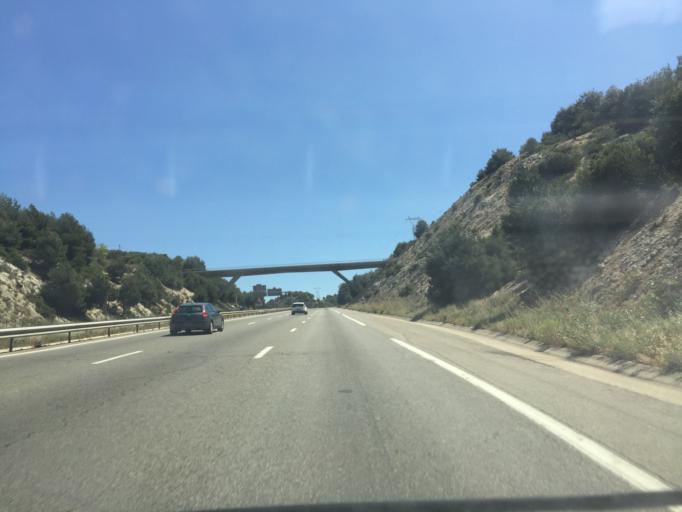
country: FR
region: Provence-Alpes-Cote d'Azur
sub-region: Departement des Bouches-du-Rhone
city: Les Pennes-Mirabeau
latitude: 43.3904
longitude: 5.3024
